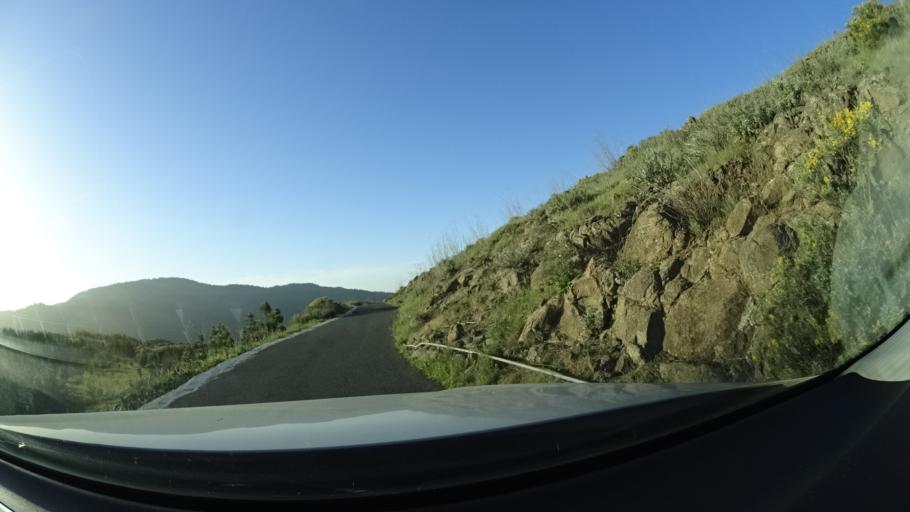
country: ES
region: Canary Islands
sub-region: Provincia de Las Palmas
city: Artenara
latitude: 28.0350
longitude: -15.6541
